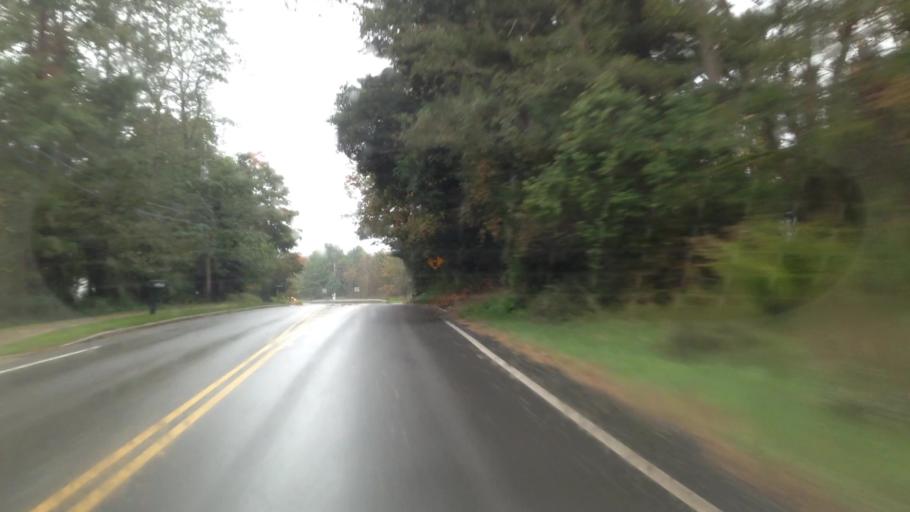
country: US
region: Ohio
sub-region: Summit County
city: Hudson
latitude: 41.2615
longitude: -81.4084
